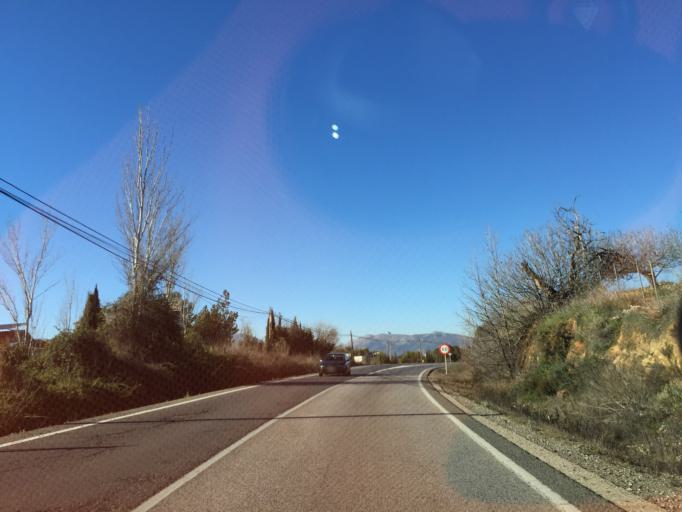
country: ES
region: Andalusia
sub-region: Provincia de Malaga
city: Arriate
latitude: 36.7650
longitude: -5.1317
